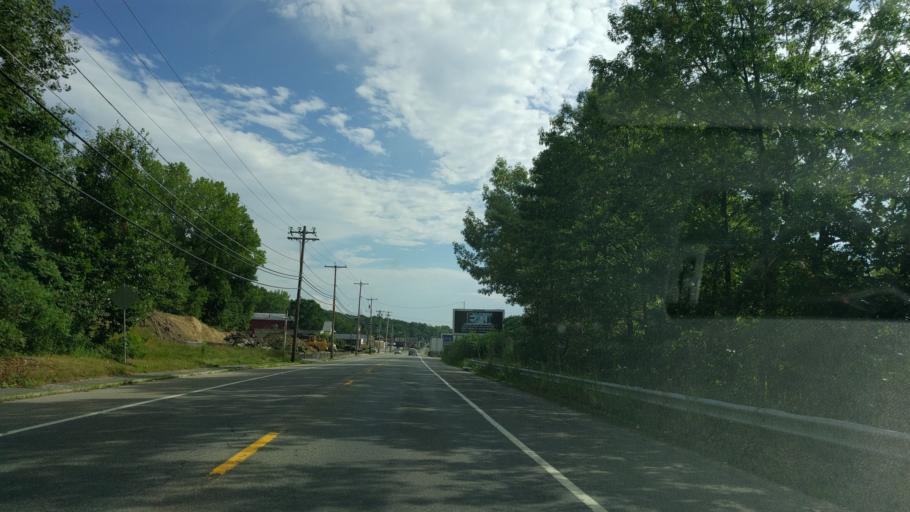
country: US
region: Massachusetts
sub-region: Worcester County
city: Auburn
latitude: 42.2272
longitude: -71.8213
